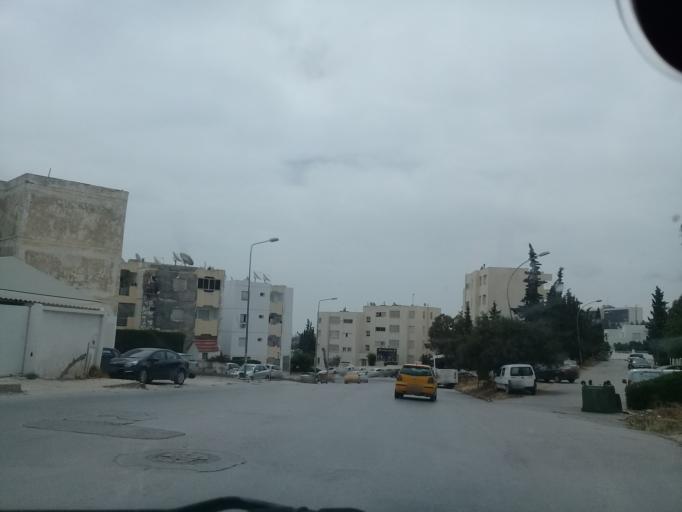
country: TN
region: Tunis
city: Tunis
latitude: 36.8379
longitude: 10.1541
